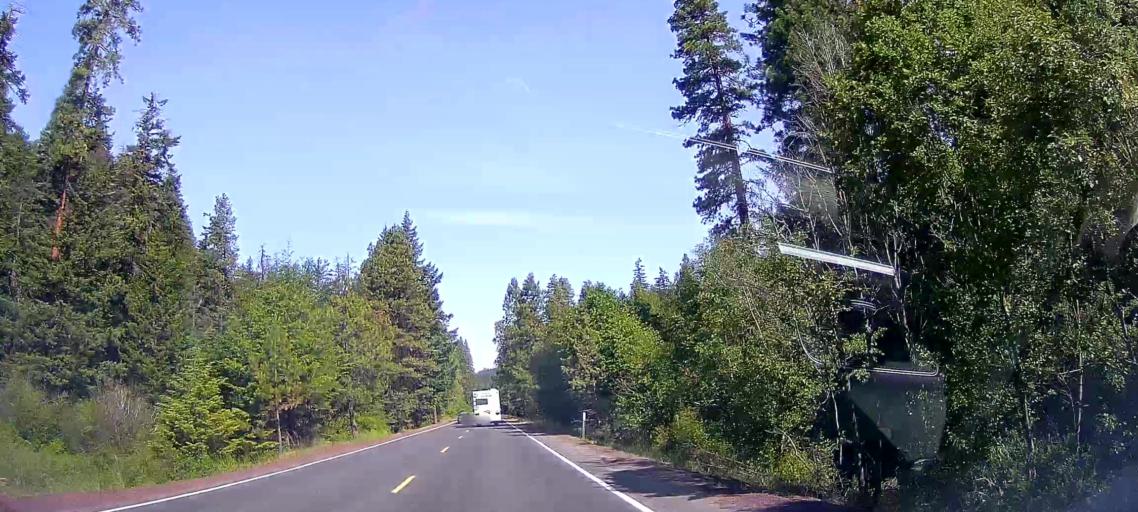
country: US
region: Oregon
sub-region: Jefferson County
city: Warm Springs
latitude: 45.0638
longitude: -121.5212
